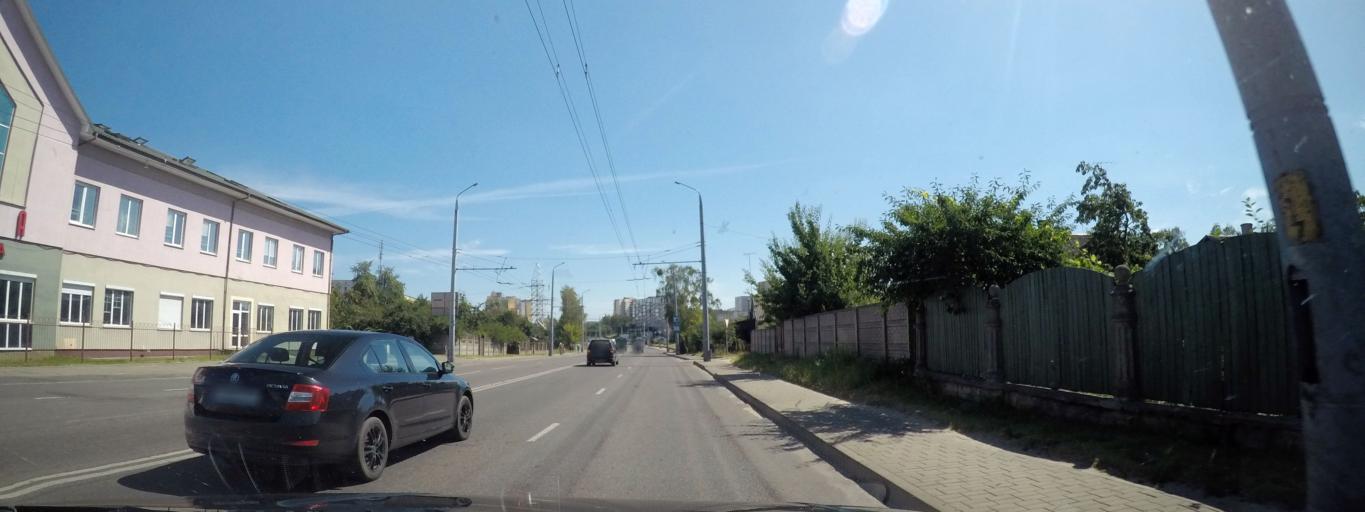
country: BY
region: Grodnenskaya
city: Hrodna
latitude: 53.6616
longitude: 23.8318
